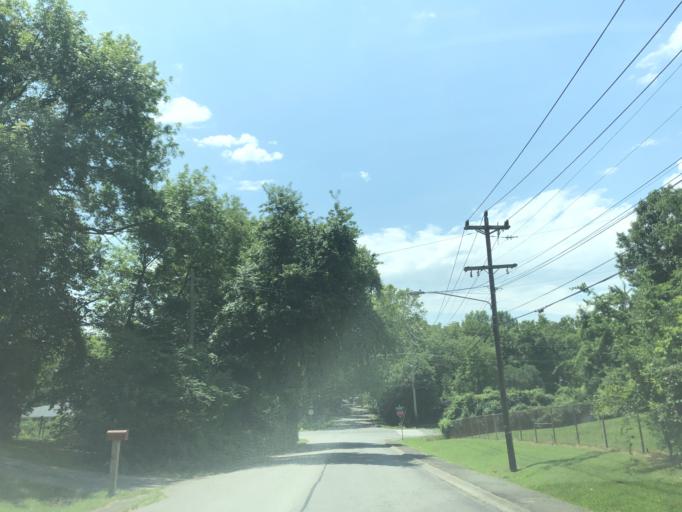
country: US
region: Tennessee
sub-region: Davidson County
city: Lakewood
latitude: 36.1542
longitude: -86.6512
